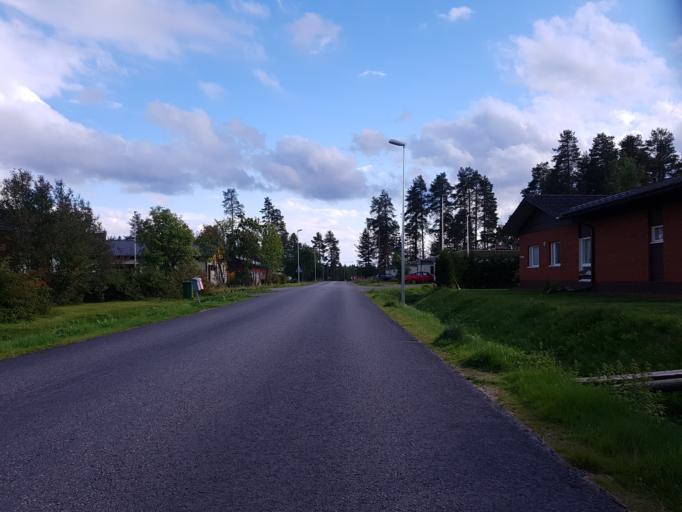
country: FI
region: Kainuu
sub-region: Kehys-Kainuu
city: Kuhmo
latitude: 64.1196
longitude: 29.5355
